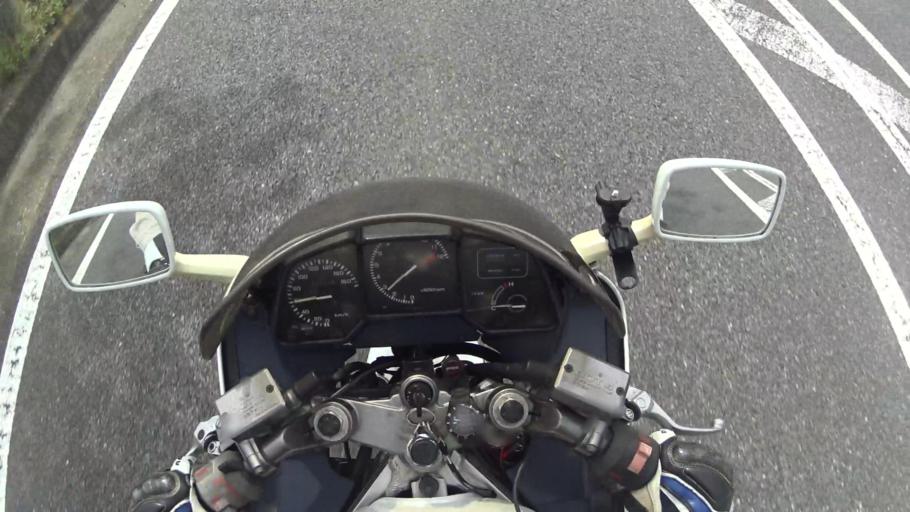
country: JP
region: Nara
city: Nara-shi
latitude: 34.7297
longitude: 135.8150
